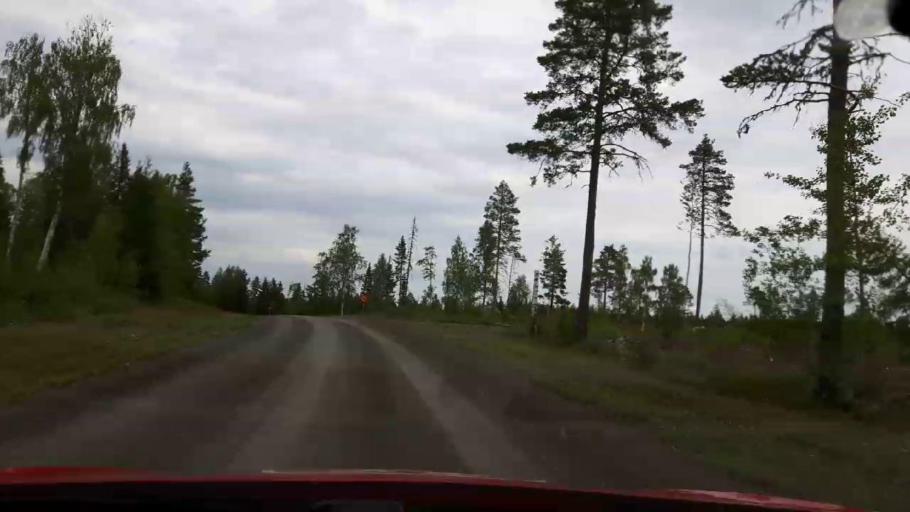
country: SE
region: Jaemtland
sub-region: Stroemsunds Kommun
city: Stroemsund
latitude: 63.8144
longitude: 15.6251
